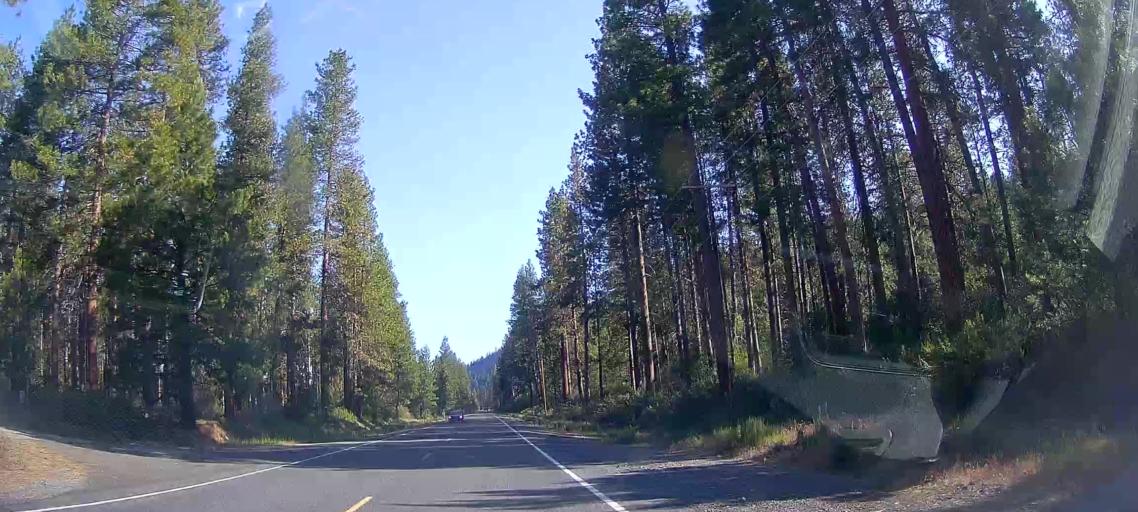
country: US
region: Oregon
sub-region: Klamath County
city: Klamath Falls
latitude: 42.6208
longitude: -121.9336
